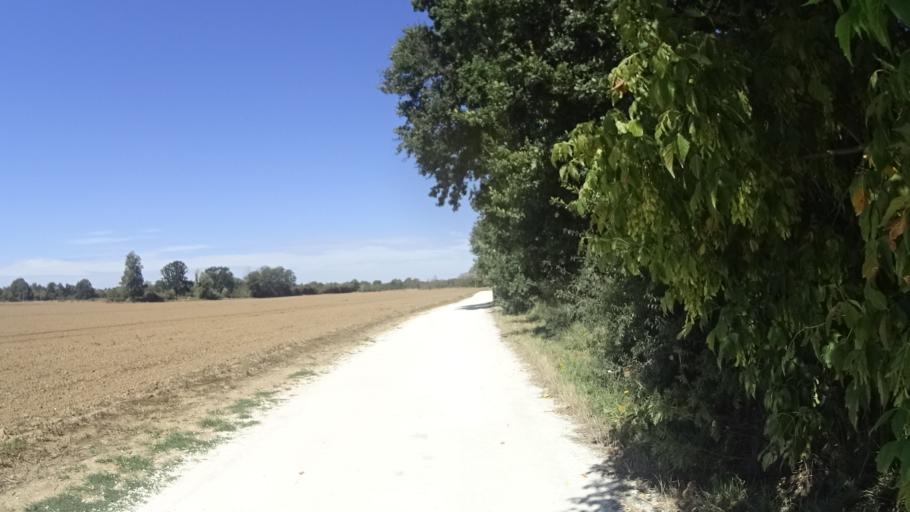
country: FR
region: Bourgogne
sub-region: Departement de la Nievre
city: Neuvy-sur-Loire
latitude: 47.5298
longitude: 2.8549
